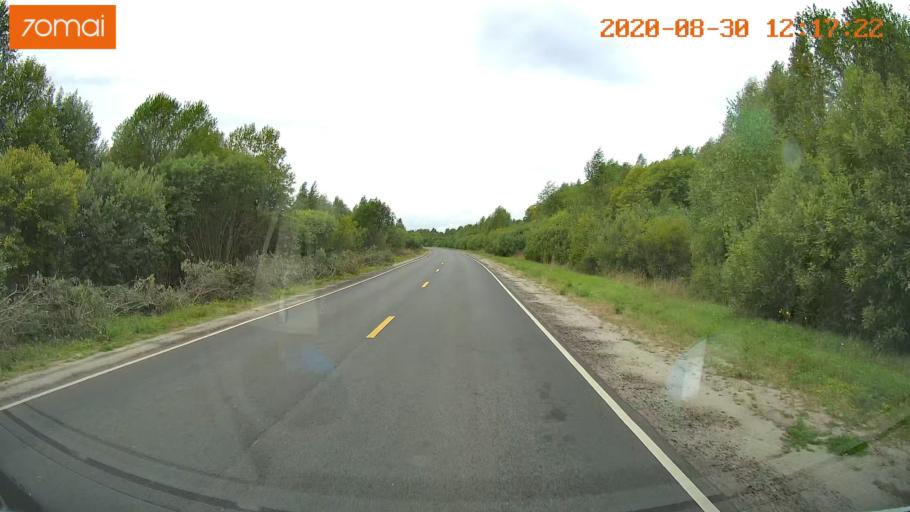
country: RU
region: Ivanovo
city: Yur'yevets
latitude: 57.3232
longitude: 42.9798
